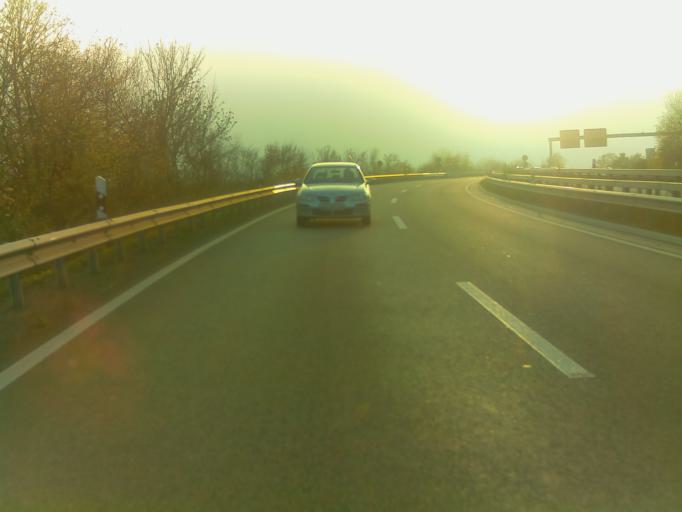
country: DE
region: Rheinland-Pfalz
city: Mutterstadt
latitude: 49.4553
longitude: 8.3604
